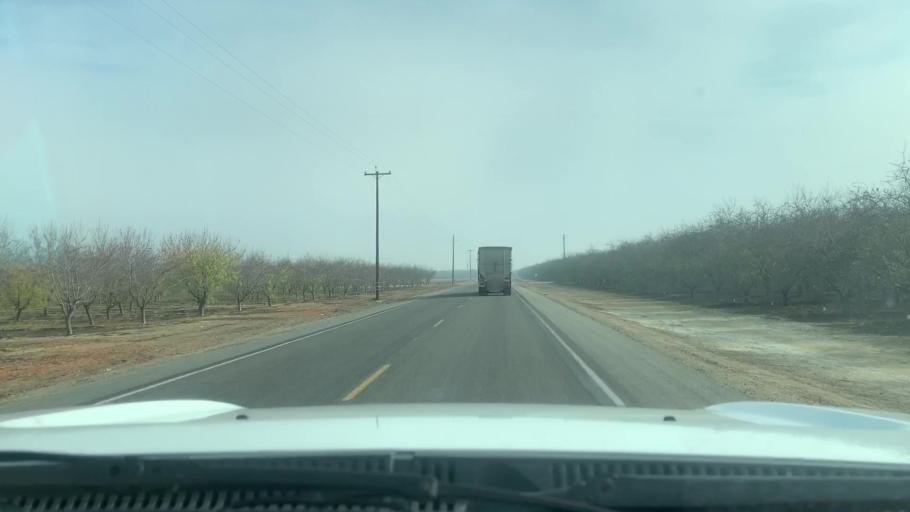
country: US
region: California
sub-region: Kern County
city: Buttonwillow
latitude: 35.5003
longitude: -119.4099
